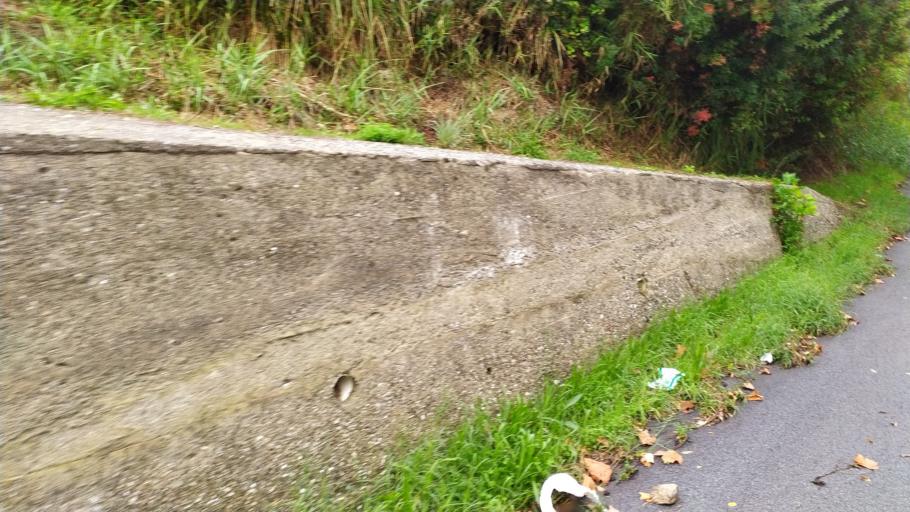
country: IT
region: Sicily
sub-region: Messina
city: Villafranca Tirrena
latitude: 38.2238
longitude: 15.4593
